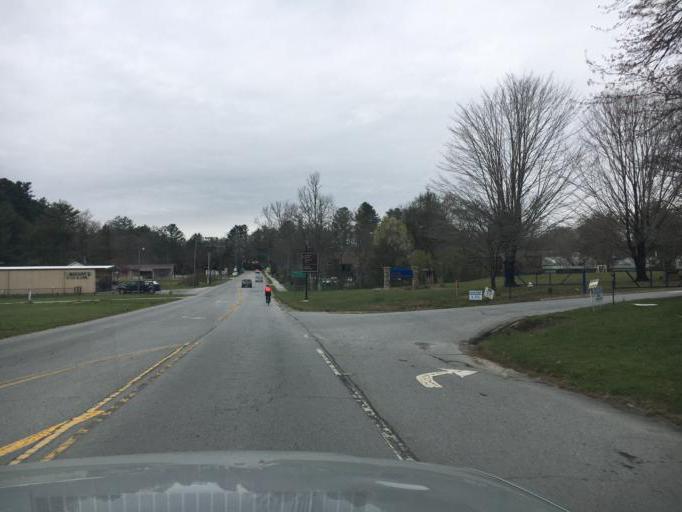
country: US
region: North Carolina
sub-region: Transylvania County
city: Brevard
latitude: 35.2245
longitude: -82.7235
